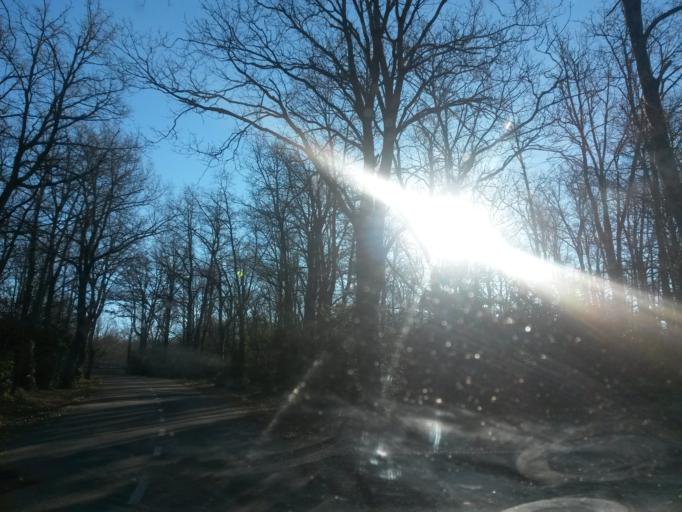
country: ES
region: Catalonia
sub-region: Provincia de Girona
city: les Planes d'Hostoles
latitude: 42.0271
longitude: 2.5323
